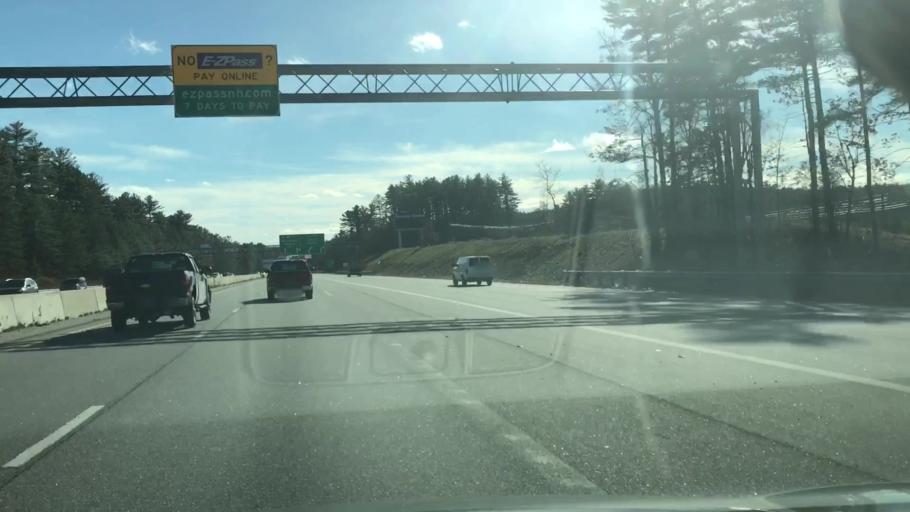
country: US
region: New Hampshire
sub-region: Merrimack County
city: Hooksett
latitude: 43.0775
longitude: -71.4724
